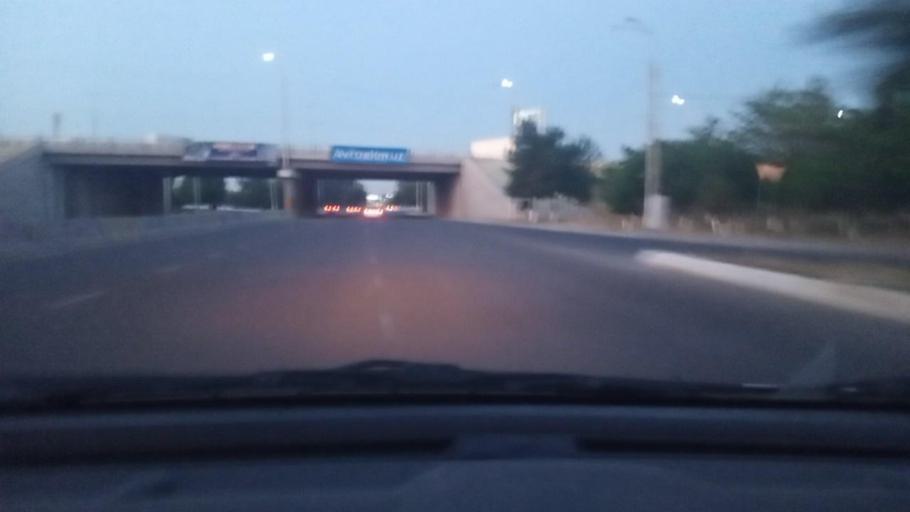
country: UZ
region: Toshkent Shahri
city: Tashkent
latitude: 41.2445
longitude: 69.2178
